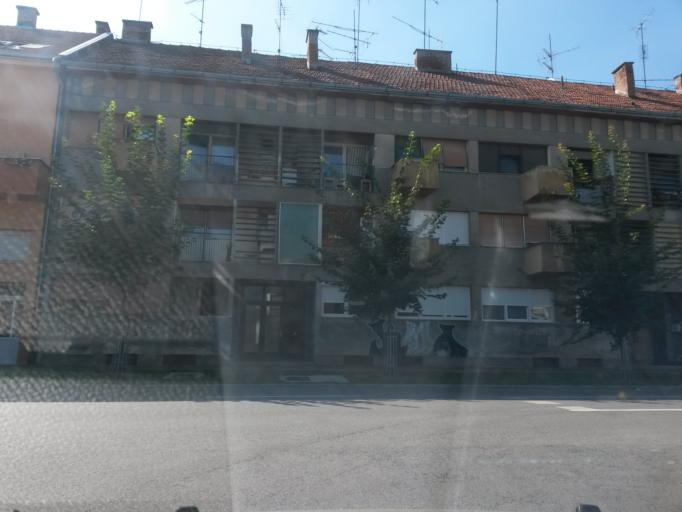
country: HR
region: Osjecko-Baranjska
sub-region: Grad Osijek
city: Osijek
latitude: 45.5564
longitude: 18.6938
